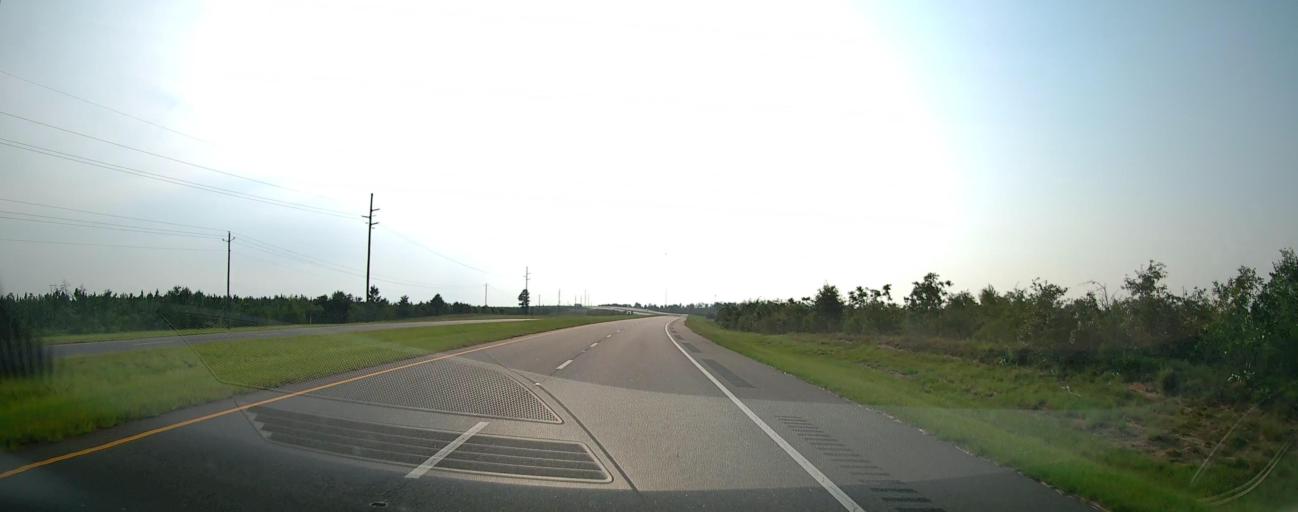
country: US
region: Georgia
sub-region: Talbot County
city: Talbotton
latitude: 32.5954
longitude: -84.4403
